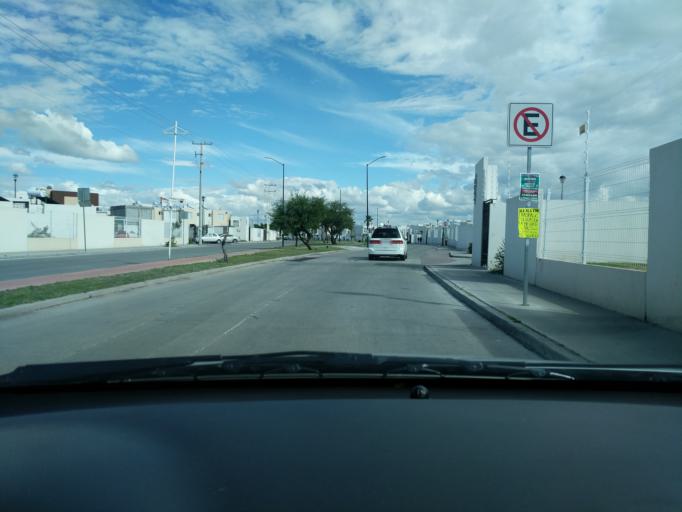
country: MX
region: Queretaro
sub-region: El Marques
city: La Loma
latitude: 20.5873
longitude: -100.2589
